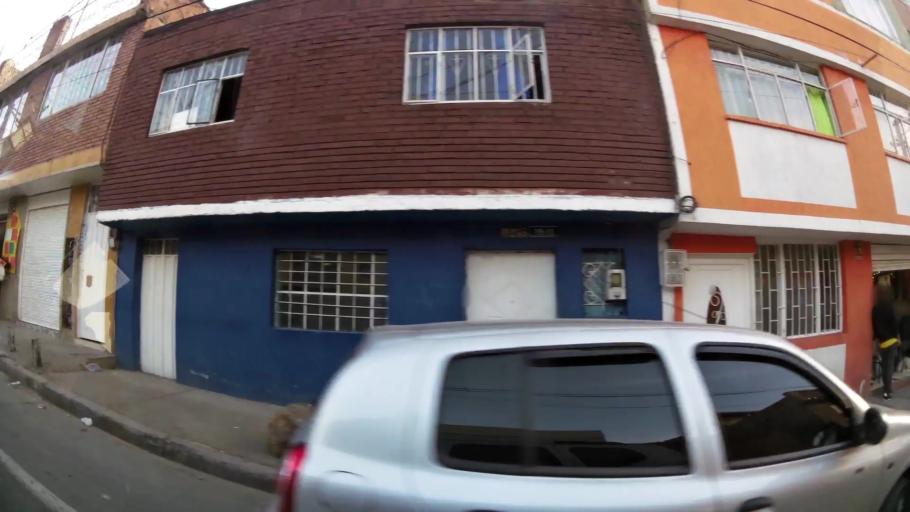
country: CO
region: Bogota D.C.
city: Bogota
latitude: 4.5641
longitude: -74.1364
